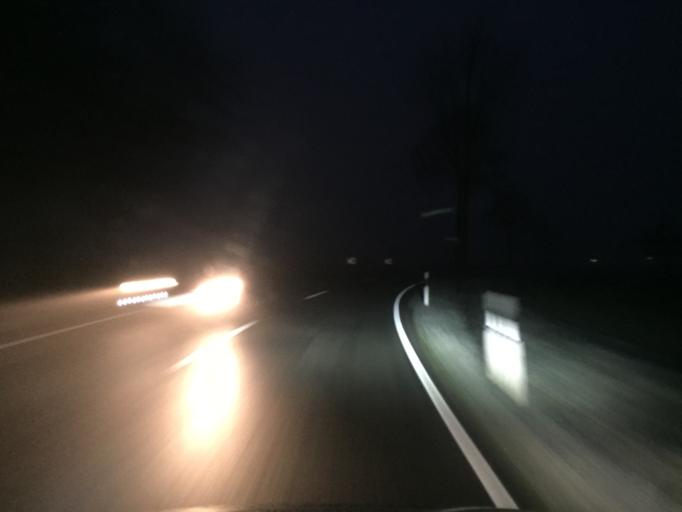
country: DE
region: Lower Saxony
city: Maasen
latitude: 52.6706
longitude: 8.8923
